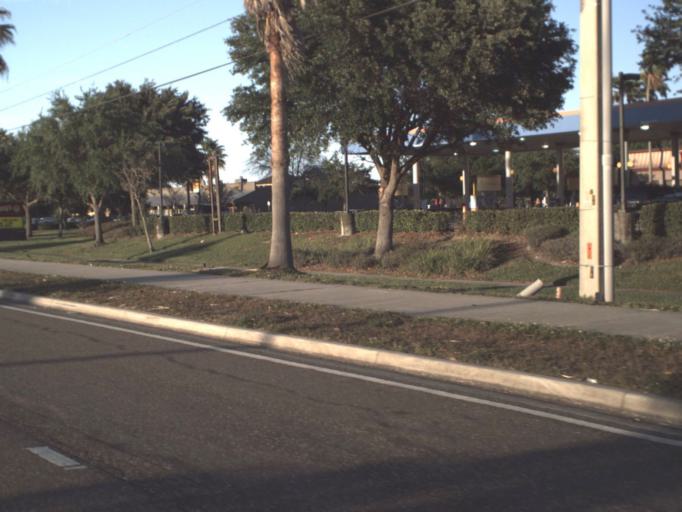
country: US
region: Florida
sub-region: Orange County
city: Conway
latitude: 28.4652
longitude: -81.3099
